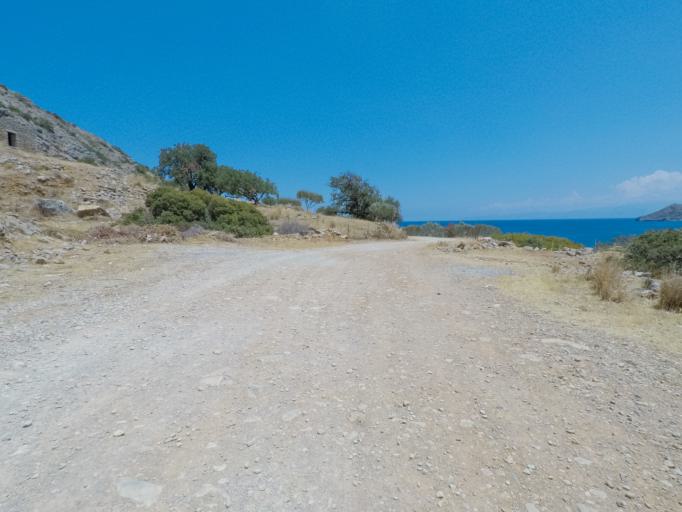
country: GR
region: Crete
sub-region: Nomos Lasithiou
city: Elounda
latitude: 35.3056
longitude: 25.7316
